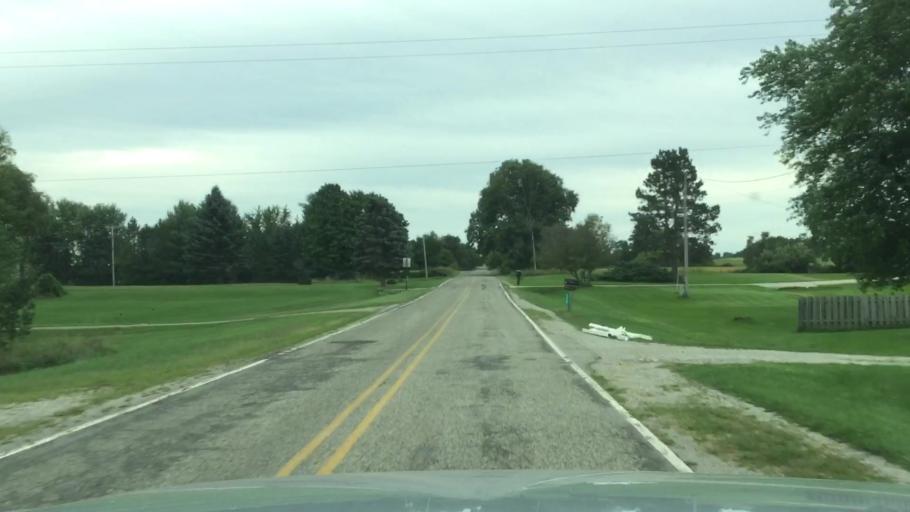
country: US
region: Michigan
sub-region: Shiawassee County
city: Durand
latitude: 42.9015
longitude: -84.0693
